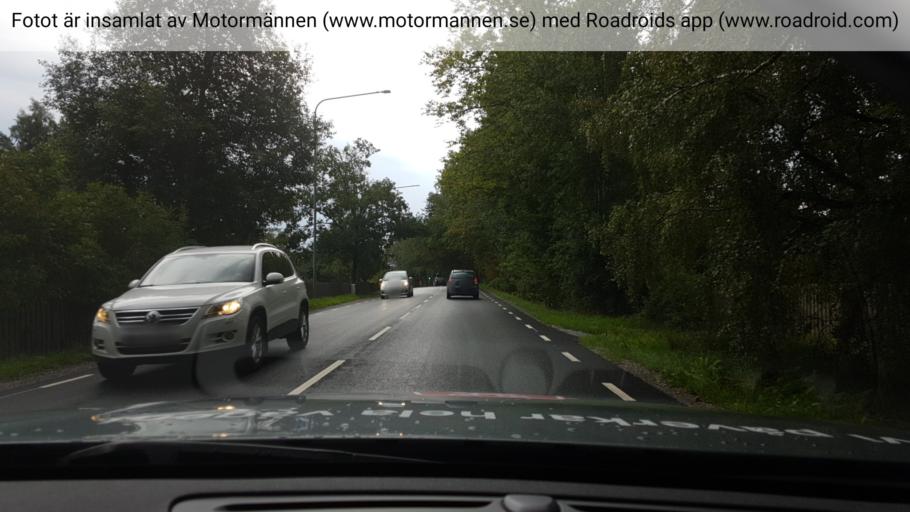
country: SE
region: Uppsala
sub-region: Habo Kommun
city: Balsta
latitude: 59.5571
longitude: 17.5456
